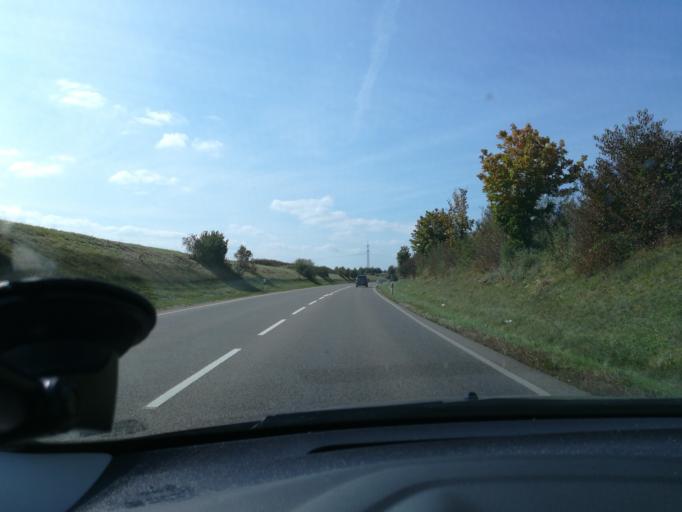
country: DE
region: Bavaria
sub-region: Upper Bavaria
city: Zorneding
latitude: 48.0762
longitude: 11.8302
